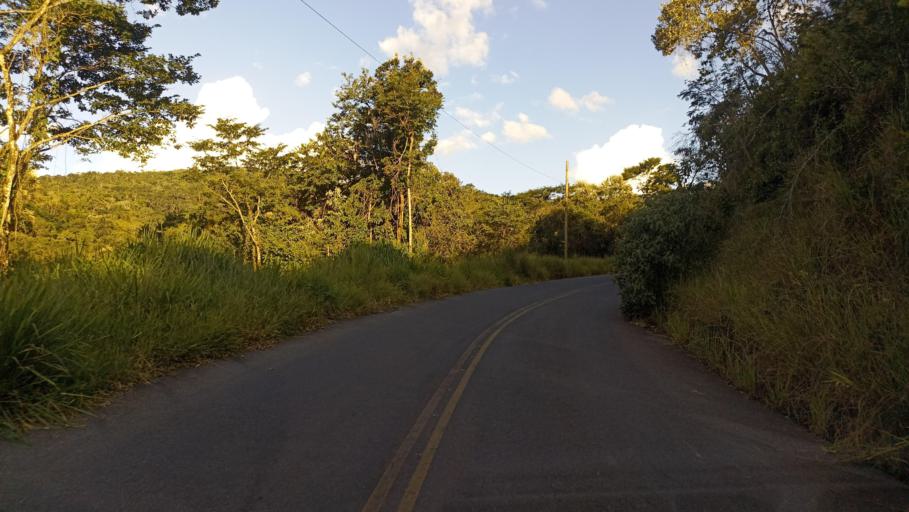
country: BR
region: Minas Gerais
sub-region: Ouro Preto
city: Ouro Preto
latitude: -20.3182
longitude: -43.6163
